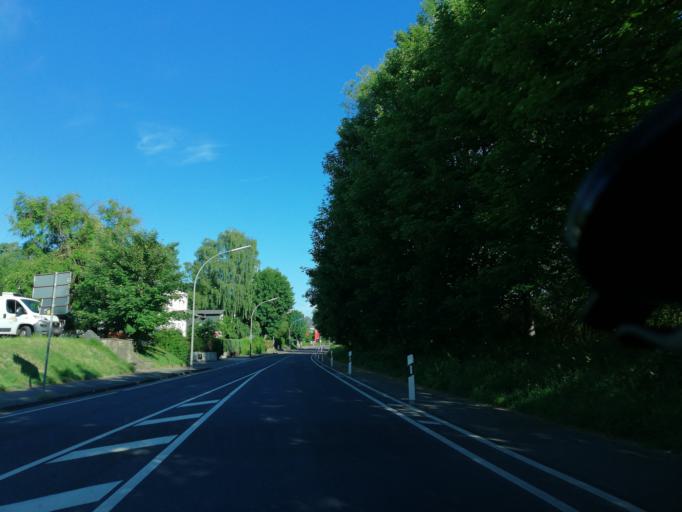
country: DE
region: North Rhine-Westphalia
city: Wetter (Ruhr)
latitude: 51.3954
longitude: 7.3548
